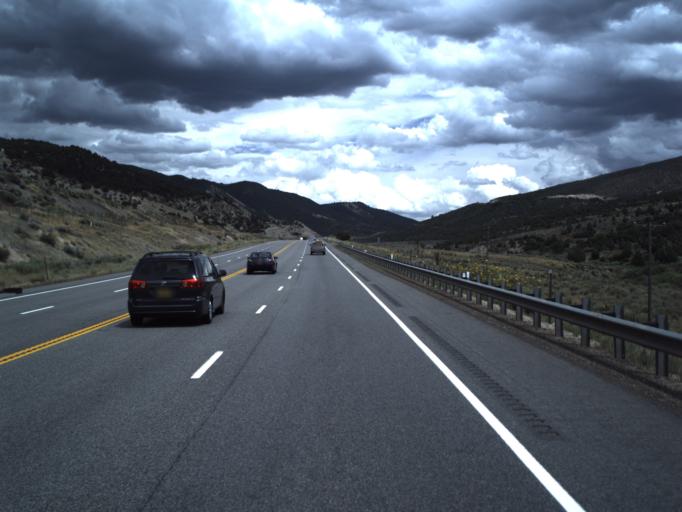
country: US
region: Utah
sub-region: Sanpete County
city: Fairview
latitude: 39.9291
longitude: -111.1813
